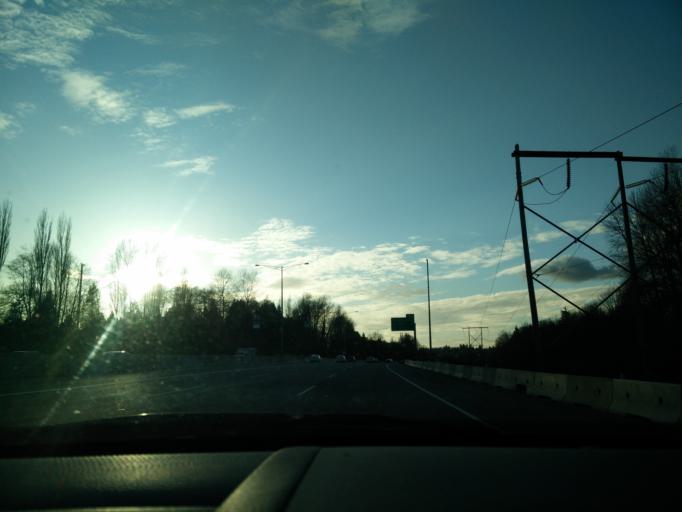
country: CA
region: British Columbia
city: Burnaby
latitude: 49.2375
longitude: -122.9451
